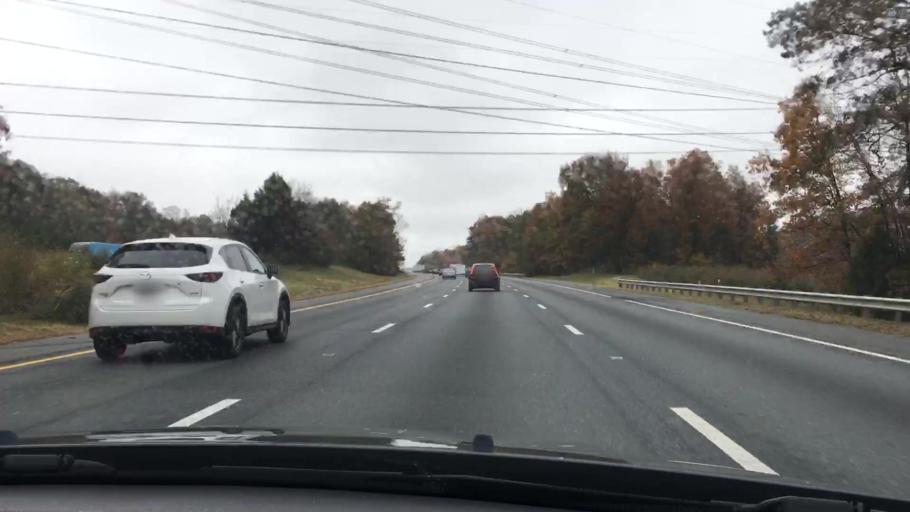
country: US
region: Virginia
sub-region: Spotsylvania County
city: Spotsylvania Courthouse
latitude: 38.0843
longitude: -77.5165
